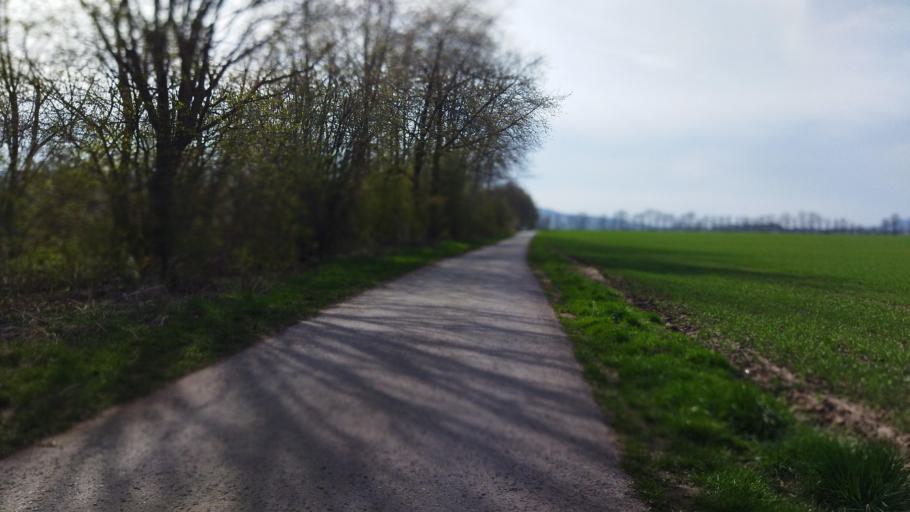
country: DE
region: Lower Saxony
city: Hessisch Oldendorf
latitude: 52.1633
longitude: 9.2268
